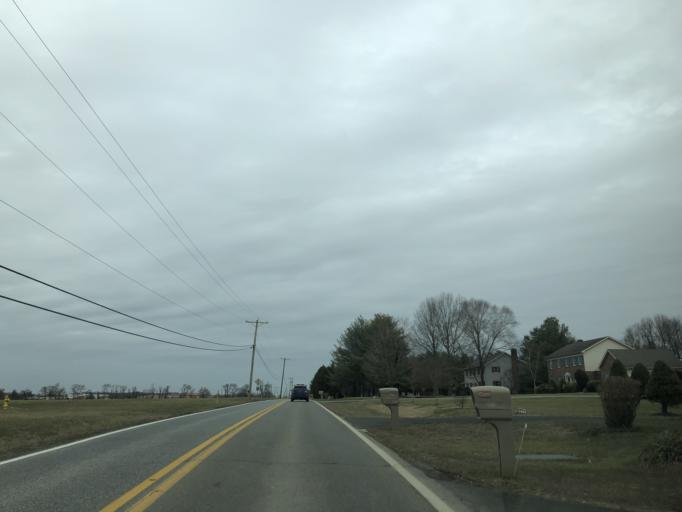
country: US
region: Delaware
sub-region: New Castle County
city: Middletown
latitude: 39.4935
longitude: -75.6890
